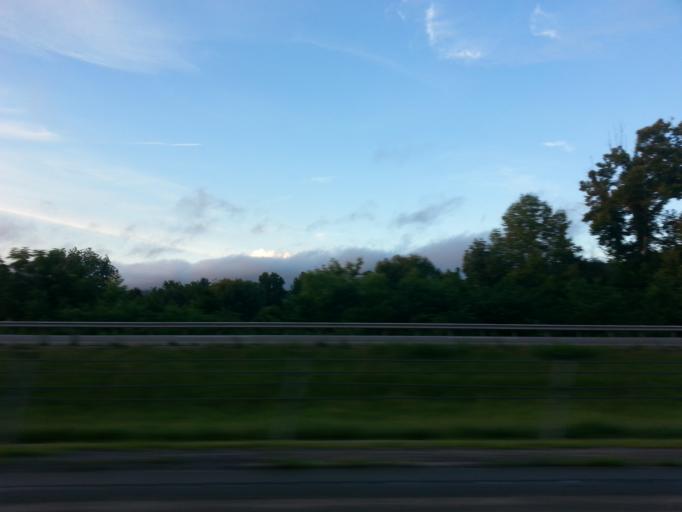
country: US
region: Kentucky
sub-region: Whitley County
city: Williamsburg
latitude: 36.7166
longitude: -84.1570
